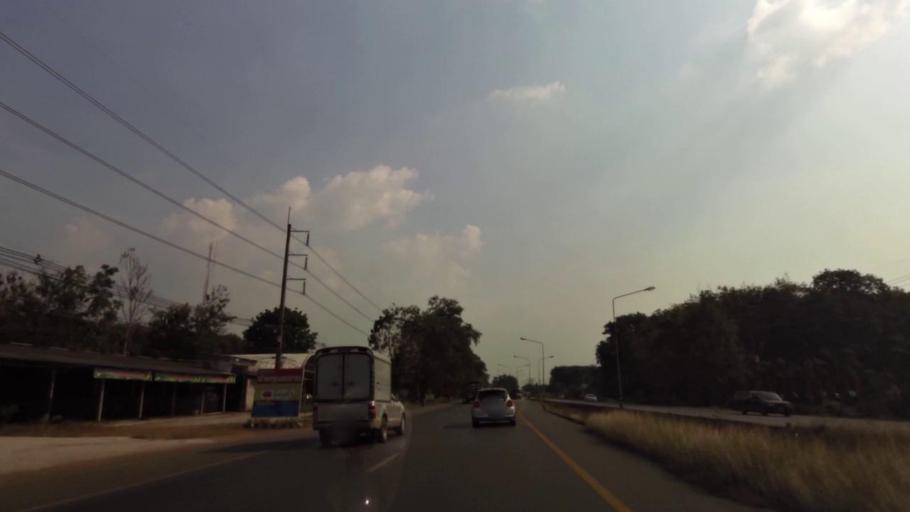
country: TH
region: Rayong
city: Wang Chan
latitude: 12.9142
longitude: 101.5330
